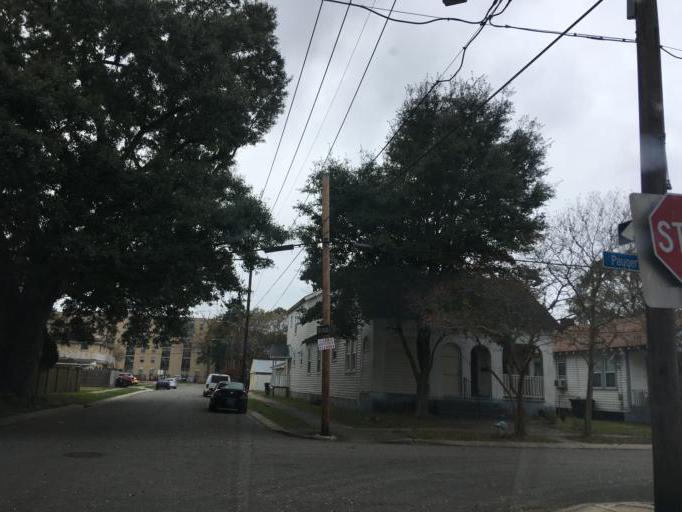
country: US
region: Louisiana
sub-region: Orleans Parish
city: New Orleans
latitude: 29.9937
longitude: -90.0623
